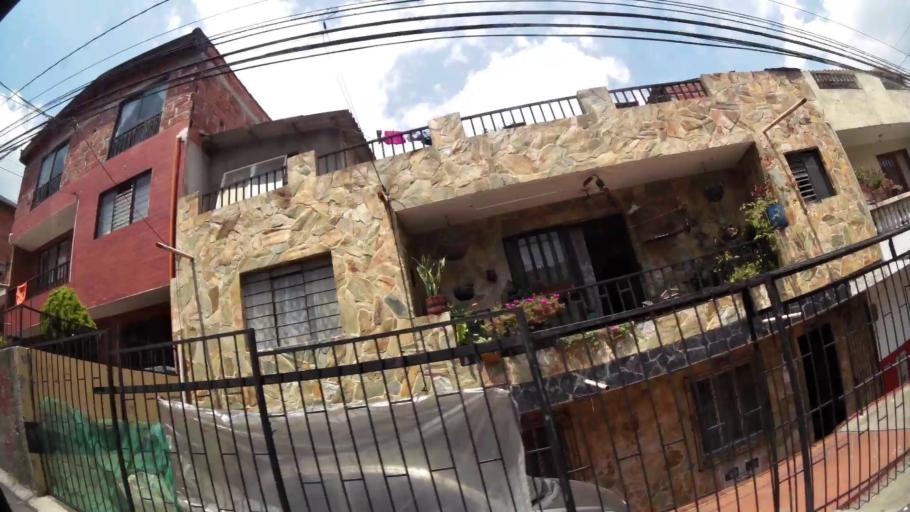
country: CO
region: Antioquia
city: Medellin
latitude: 6.2905
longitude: -75.5760
